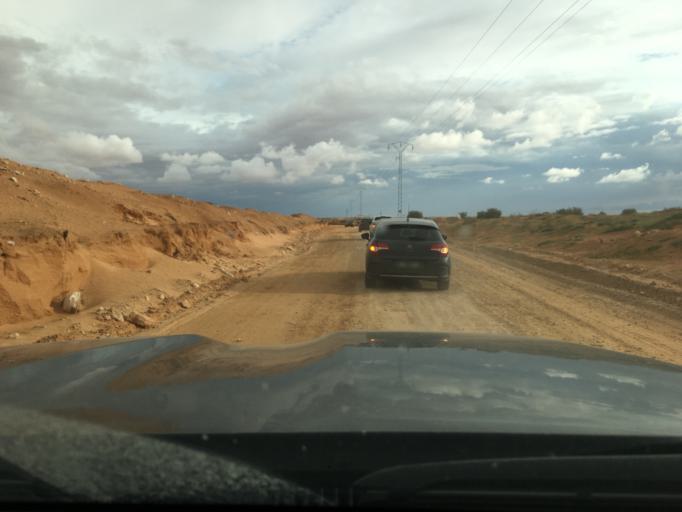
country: TN
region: Madanin
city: Medenine
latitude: 33.2719
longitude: 10.5664
